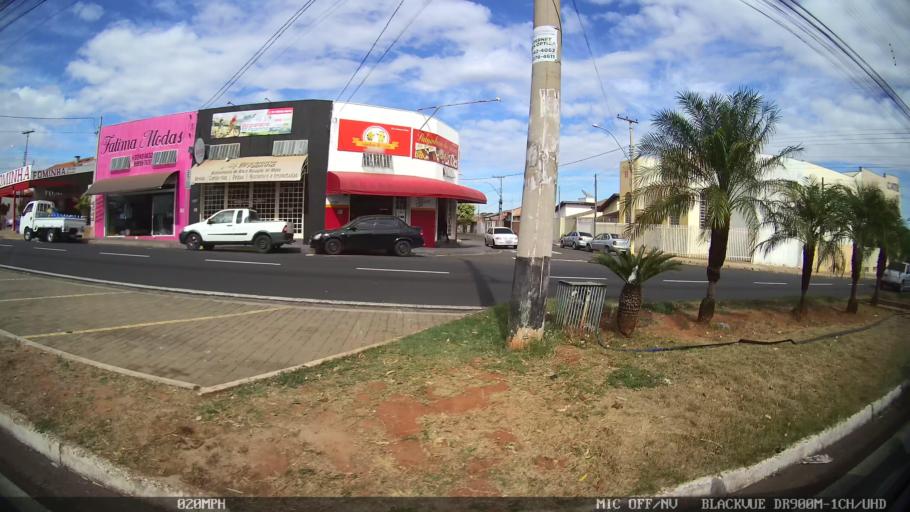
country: BR
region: Sao Paulo
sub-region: Sao Jose Do Rio Preto
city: Sao Jose do Rio Preto
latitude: -20.8039
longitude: -49.4990
